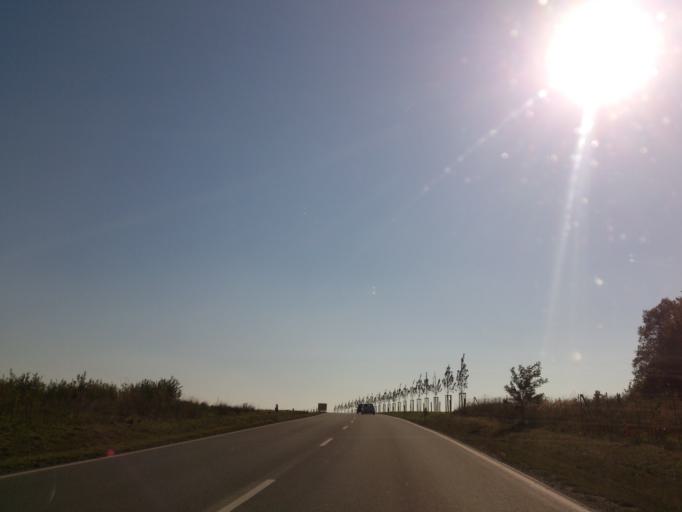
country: DE
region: Hesse
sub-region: Regierungsbezirk Kassel
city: Calden
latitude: 51.4187
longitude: 9.3715
